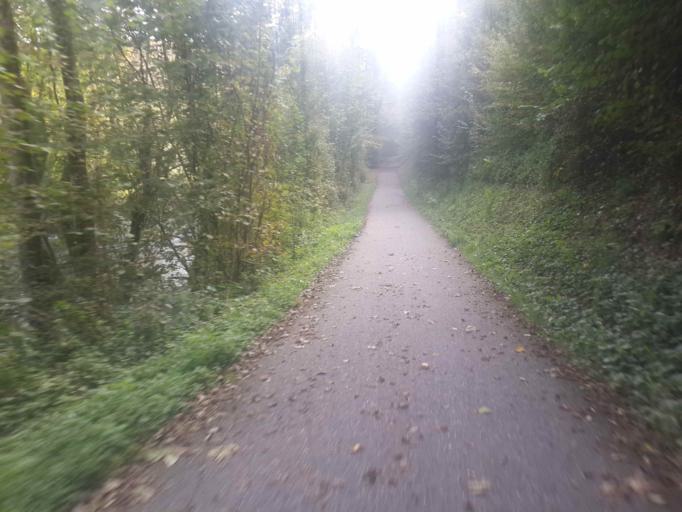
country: DE
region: Baden-Wuerttemberg
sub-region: Regierungsbezirk Stuttgart
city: Widdern
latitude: 49.3036
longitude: 9.4292
